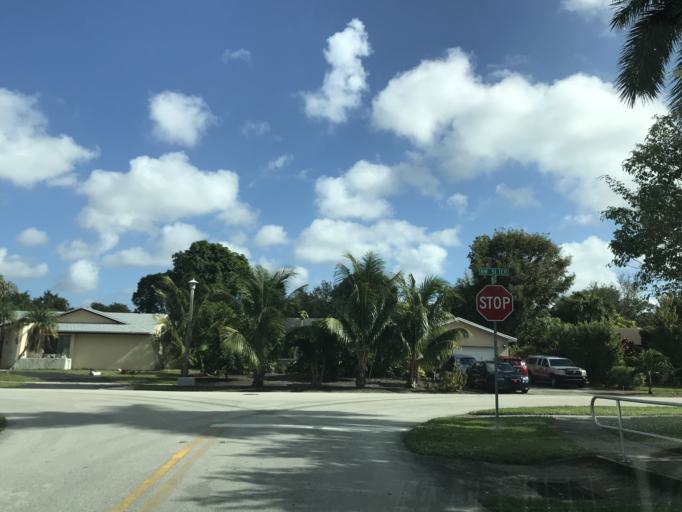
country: US
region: Florida
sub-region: Broward County
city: Coconut Creek
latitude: 26.2652
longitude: -80.1932
